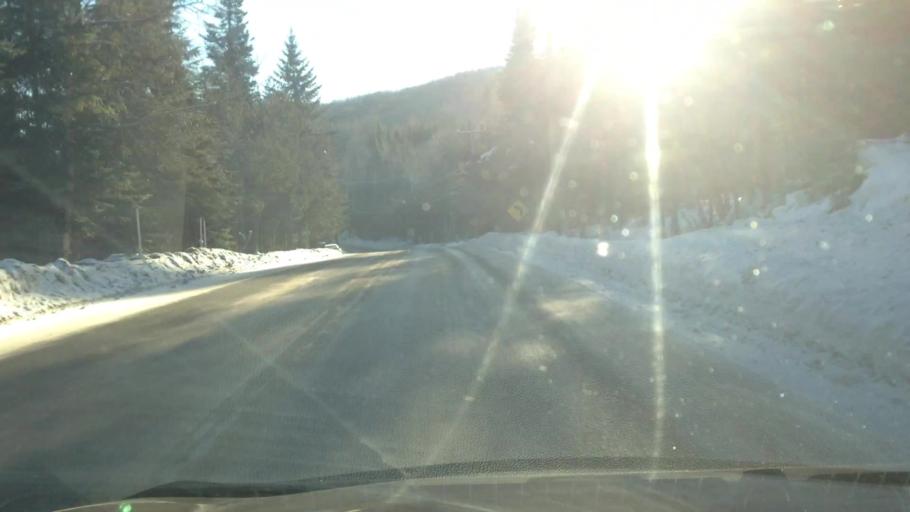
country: CA
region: Quebec
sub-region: Laurentides
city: Sainte-Agathe-des-Monts
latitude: 45.9169
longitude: -74.3737
